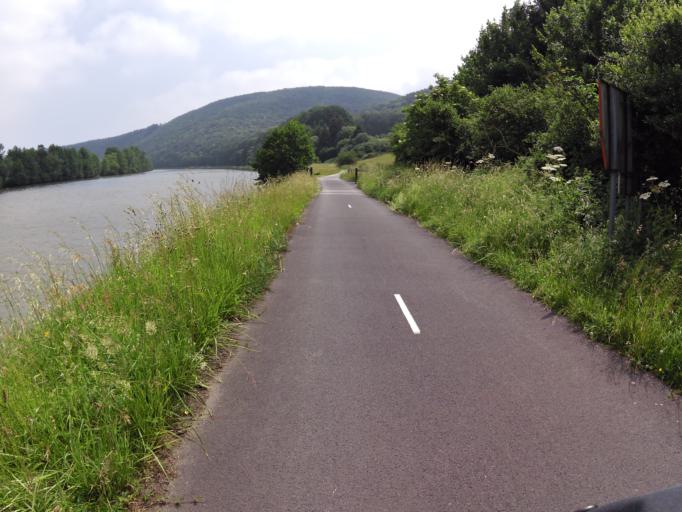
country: FR
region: Champagne-Ardenne
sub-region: Departement des Ardennes
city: Vireux-Wallerand
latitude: 50.0915
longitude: 4.7468
